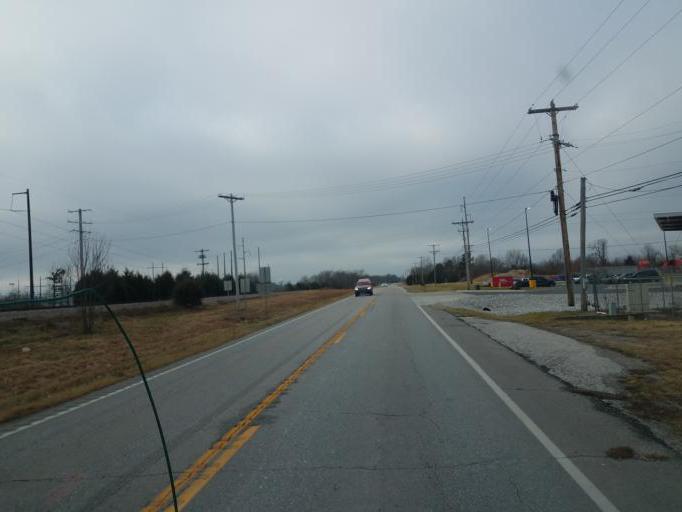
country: US
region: Missouri
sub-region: Greene County
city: Strafford
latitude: 37.2509
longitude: -93.1690
